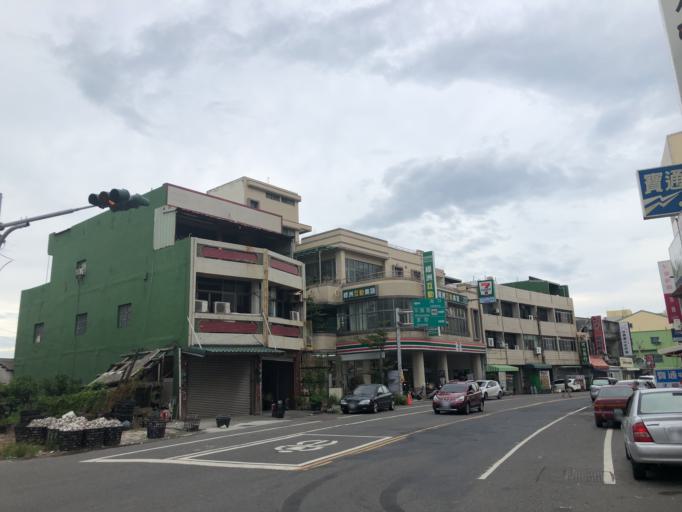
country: TW
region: Taiwan
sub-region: Chiayi
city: Taibao
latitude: 23.6990
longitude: 120.1986
